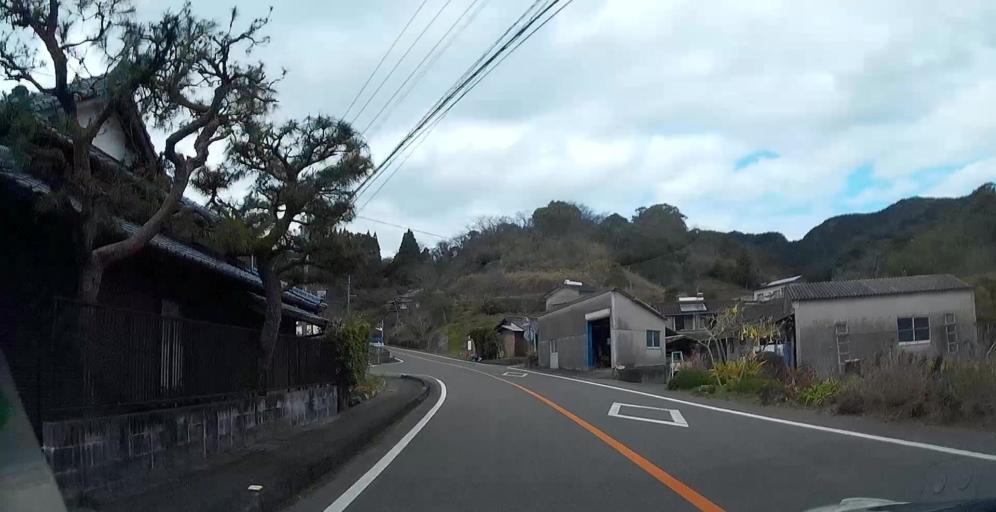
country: JP
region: Kumamoto
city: Yatsushiro
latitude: 32.3655
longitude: 130.5092
